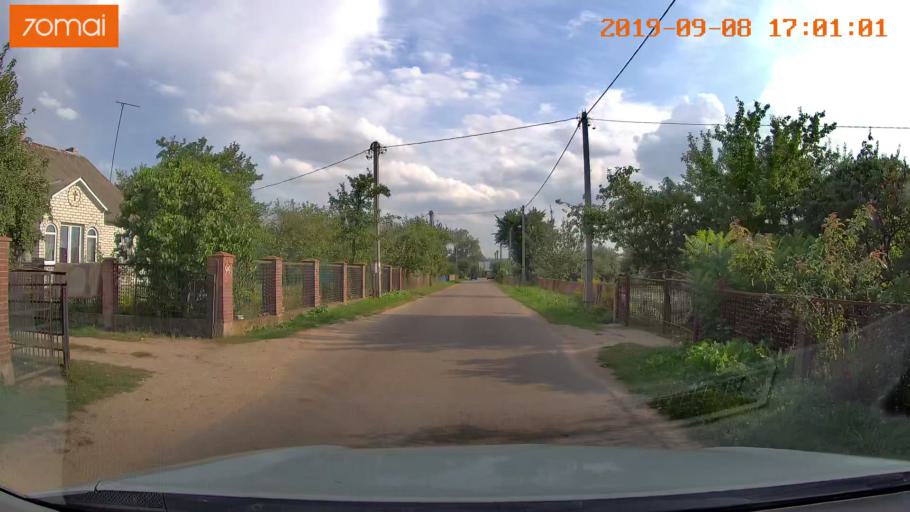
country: BY
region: Grodnenskaya
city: Hrodna
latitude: 53.7125
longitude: 23.9333
